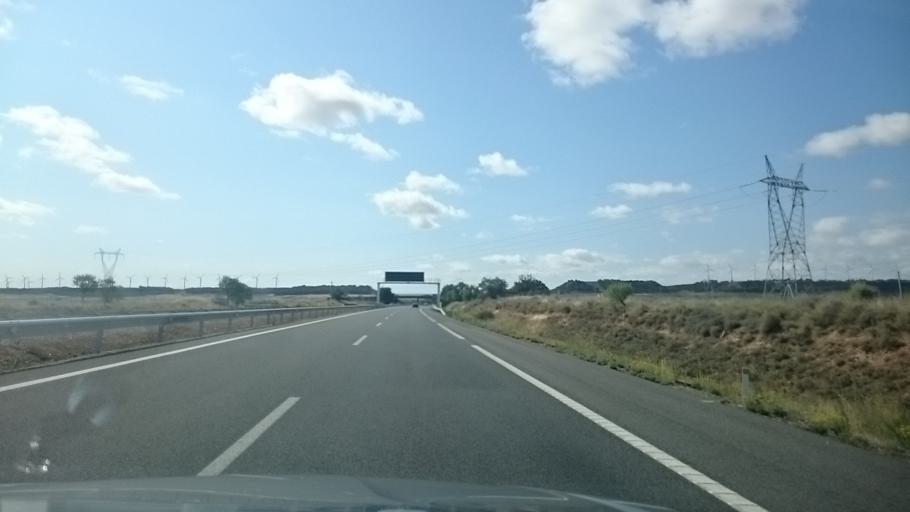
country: ES
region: Navarre
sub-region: Provincia de Navarra
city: Corella
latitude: 42.1072
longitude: -1.7298
